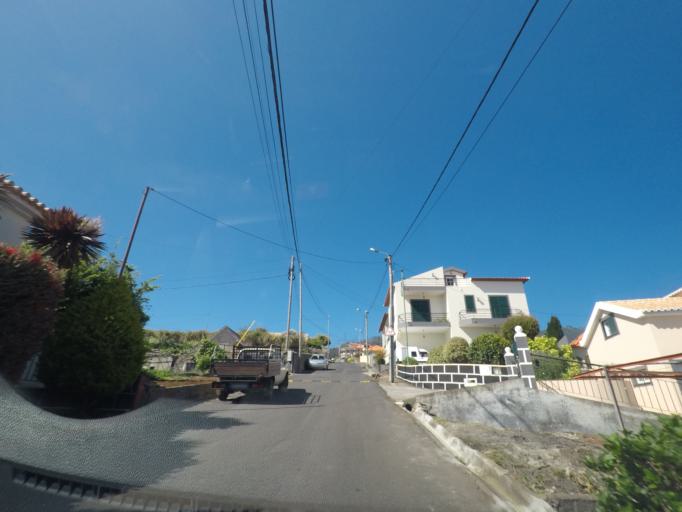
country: PT
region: Madeira
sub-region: Calheta
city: Arco da Calheta
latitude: 32.7036
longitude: -17.1164
